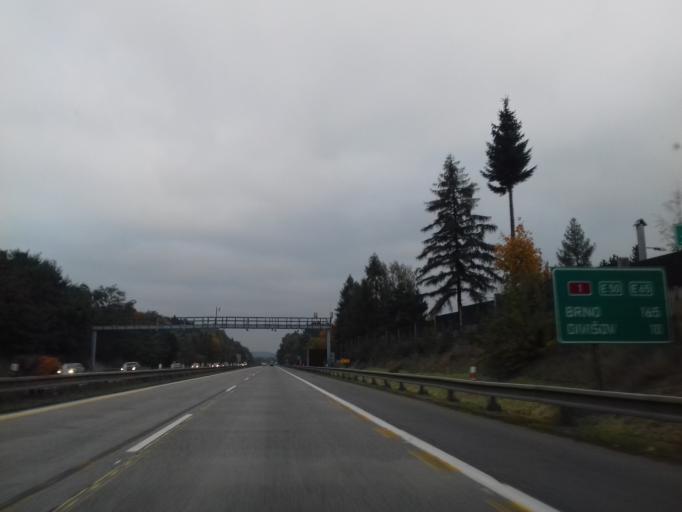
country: CZ
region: Central Bohemia
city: Divisov
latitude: 49.8376
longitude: 14.8339
